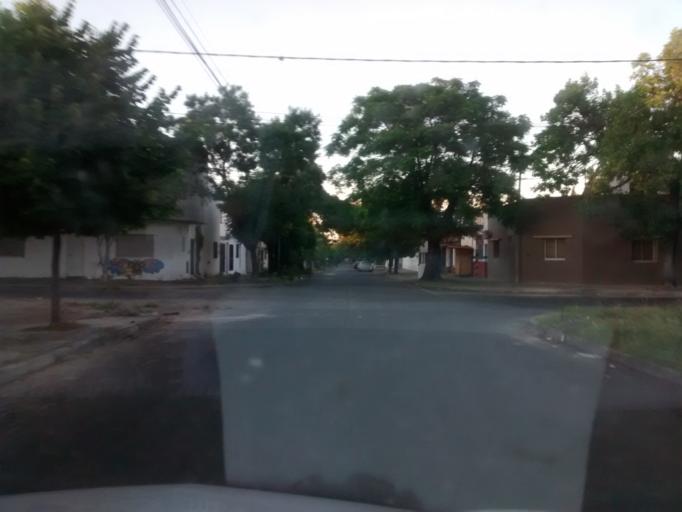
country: AR
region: Buenos Aires
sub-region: Partido de La Plata
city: La Plata
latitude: -34.9425
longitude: -57.9486
